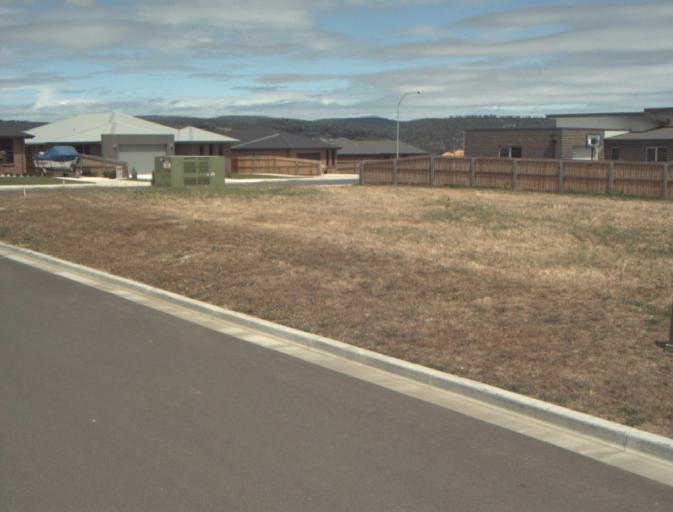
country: AU
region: Tasmania
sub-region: Launceston
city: Mayfield
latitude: -41.3816
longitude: 147.1133
